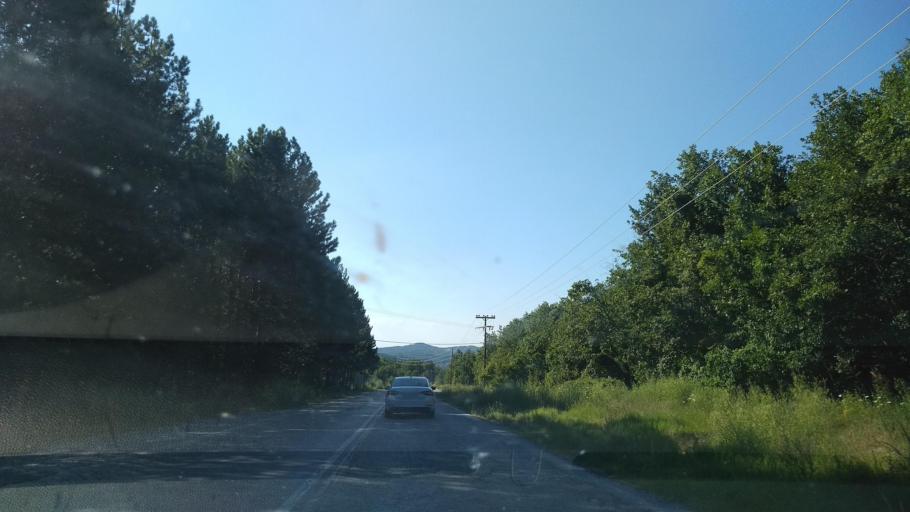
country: GR
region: Central Macedonia
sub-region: Nomos Chalkidikis
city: Megali Panagia
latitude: 40.4590
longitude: 23.6558
